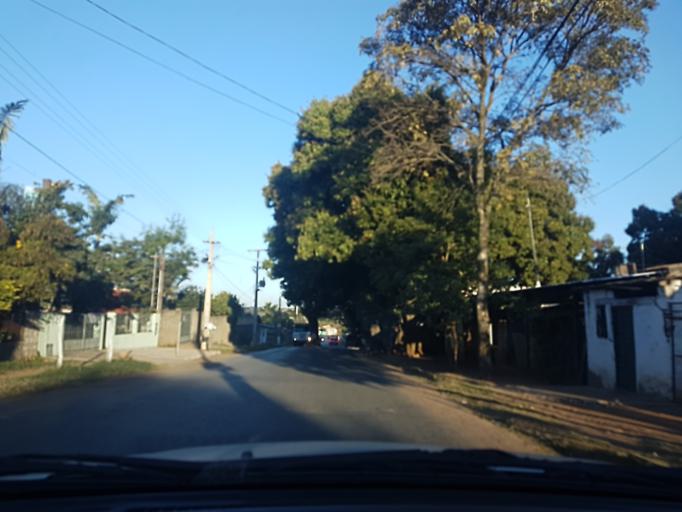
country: PY
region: Central
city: Colonia Mariano Roque Alonso
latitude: -25.2168
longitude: -57.5219
